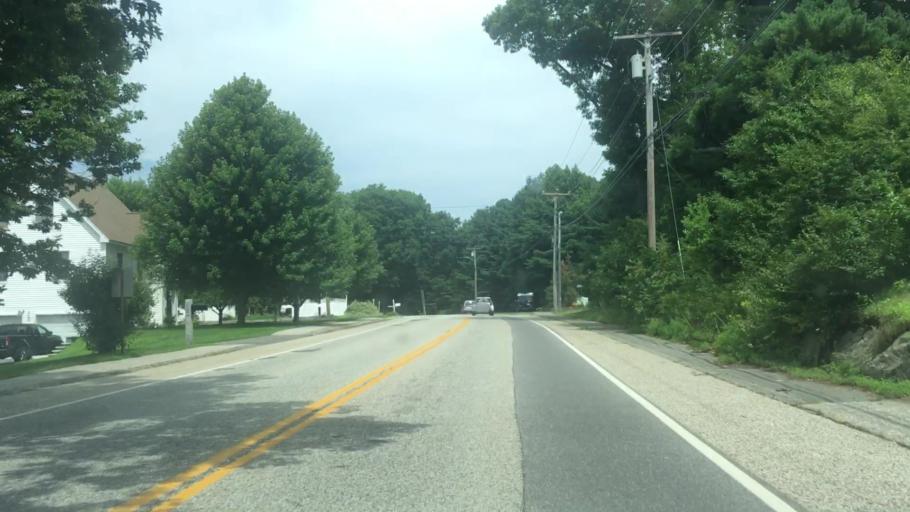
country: US
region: Maine
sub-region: Cumberland County
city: South Portland Gardens
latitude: 43.6088
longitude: -70.2819
